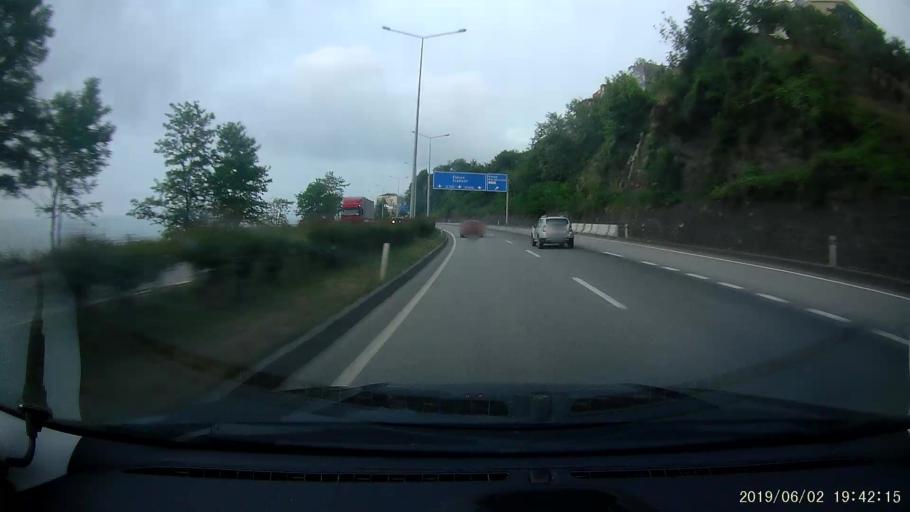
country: TR
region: Giresun
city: Kesap
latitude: 40.9155
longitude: 38.4999
